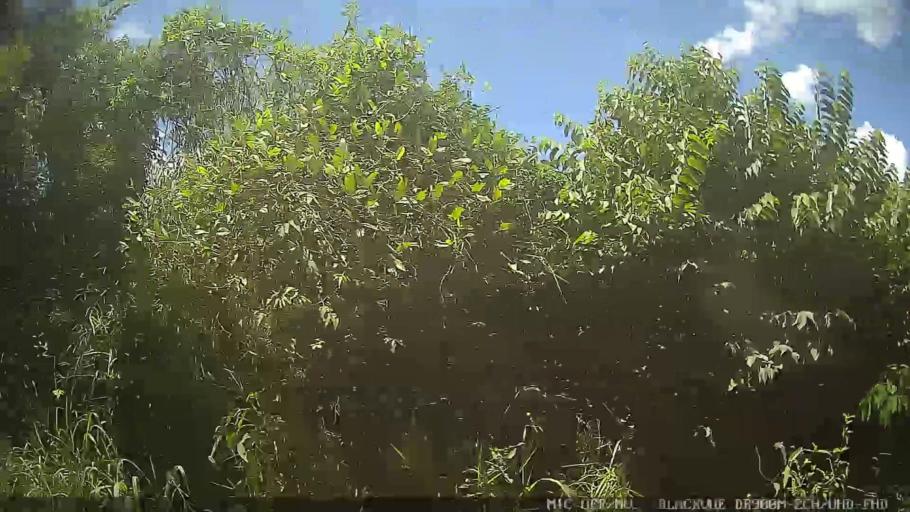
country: BR
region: Sao Paulo
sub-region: Braganca Paulista
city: Braganca Paulista
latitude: -23.0291
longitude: -46.4770
